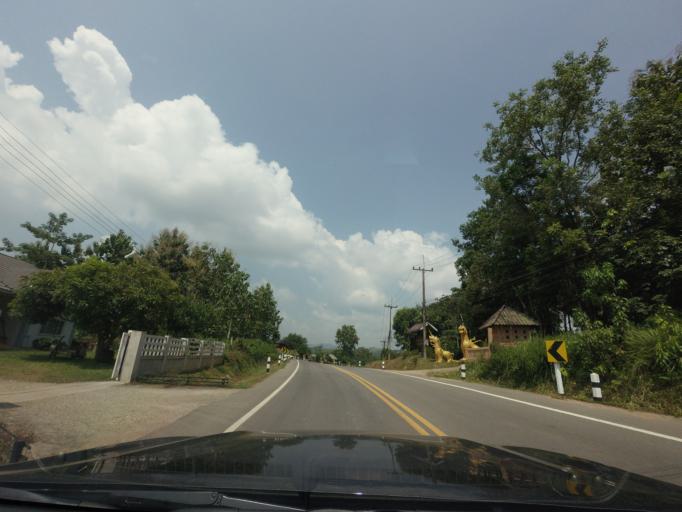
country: TH
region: Nan
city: Santi Suk
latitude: 18.9599
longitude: 100.9243
